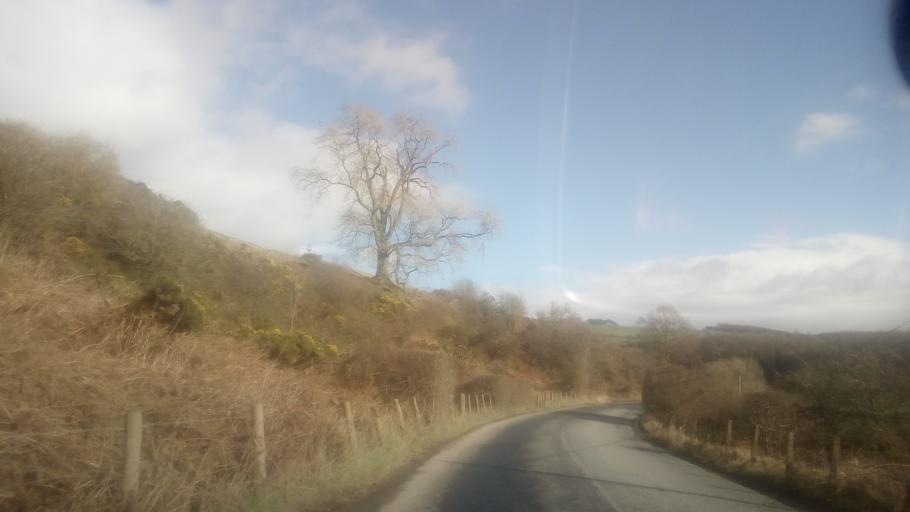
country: GB
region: Scotland
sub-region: The Scottish Borders
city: Hawick
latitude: 55.4119
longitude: -2.8404
